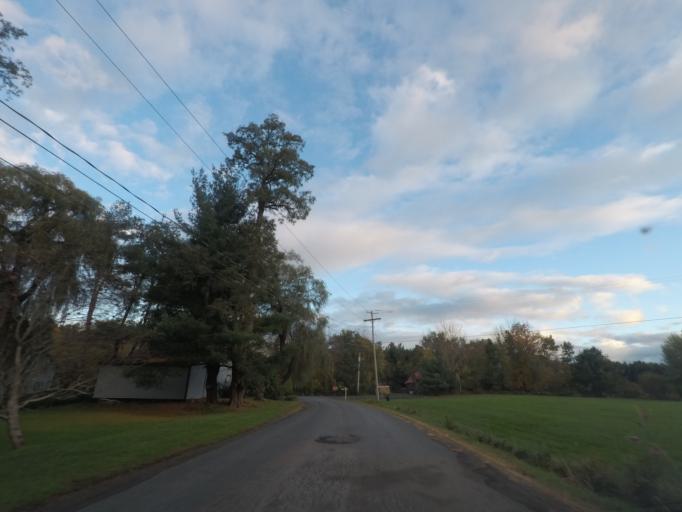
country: US
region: New York
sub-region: Rensselaer County
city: Nassau
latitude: 42.5365
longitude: -73.5756
